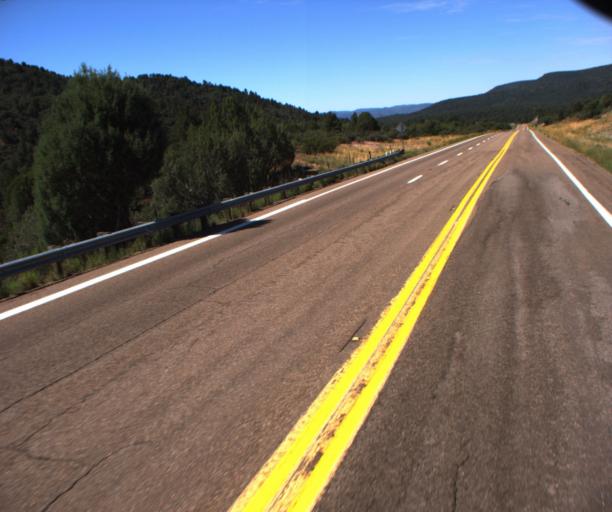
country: US
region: Arizona
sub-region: Navajo County
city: Cibecue
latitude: 33.8711
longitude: -110.4030
